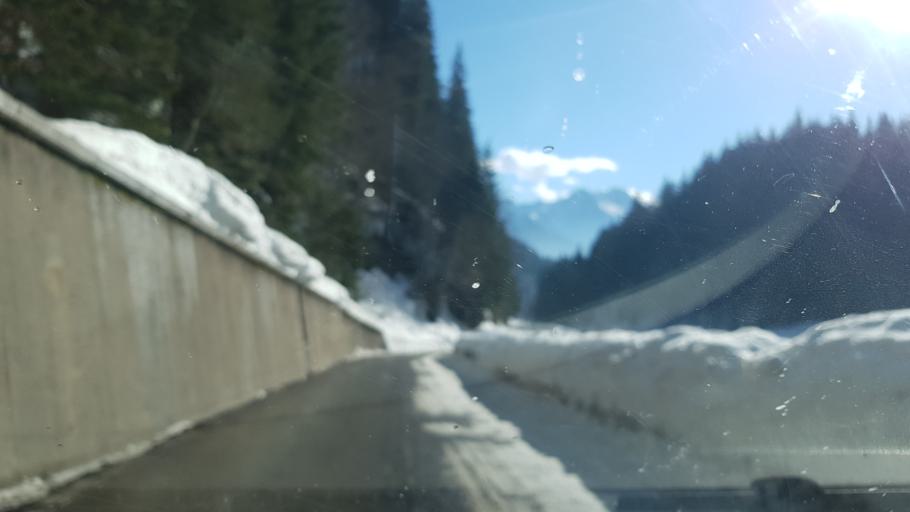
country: IT
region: Friuli Venezia Giulia
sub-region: Provincia di Udine
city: Malborghetto
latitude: 46.5408
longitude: 13.4740
